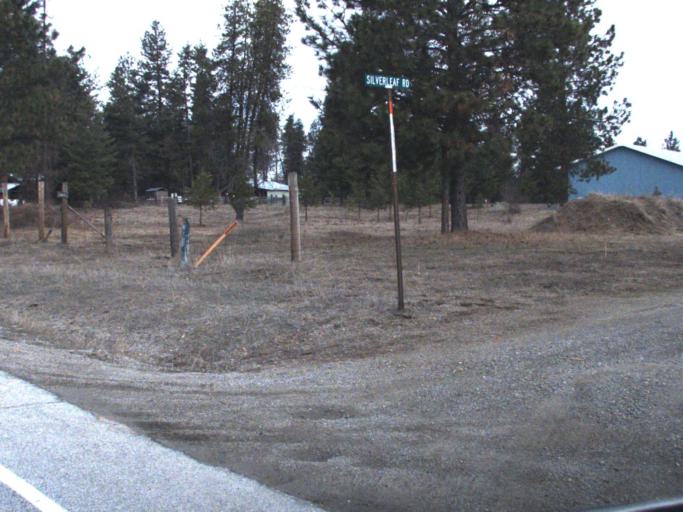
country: US
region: Washington
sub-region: Pend Oreille County
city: Newport
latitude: 48.2251
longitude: -117.1298
